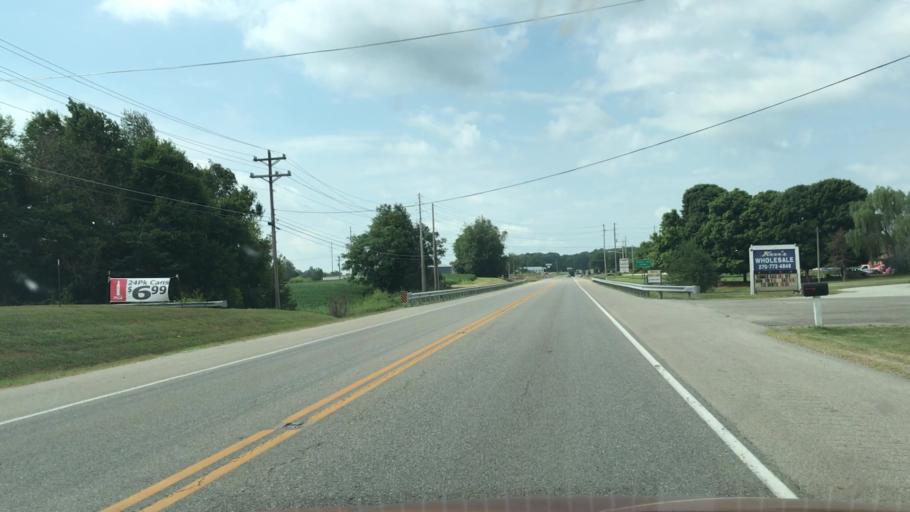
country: US
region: Kentucky
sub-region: Barren County
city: Cave City
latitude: 37.1233
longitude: -85.9618
